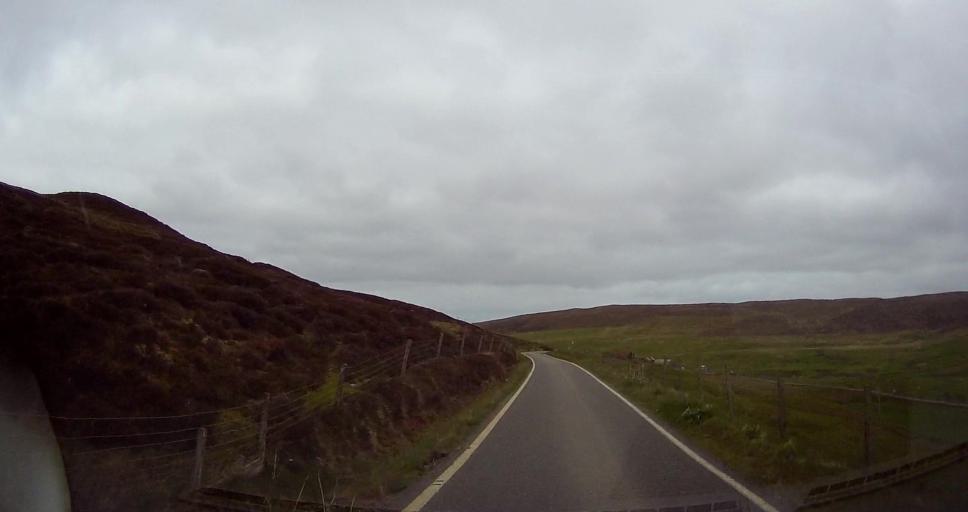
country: GB
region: Scotland
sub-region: Shetland Islands
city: Lerwick
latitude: 60.3428
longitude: -1.2827
